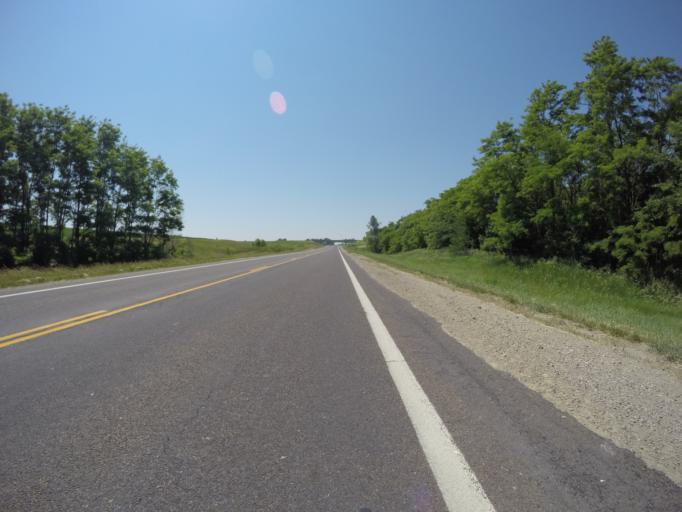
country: US
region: Kansas
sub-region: Doniphan County
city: Highland
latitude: 39.8433
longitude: -95.2652
